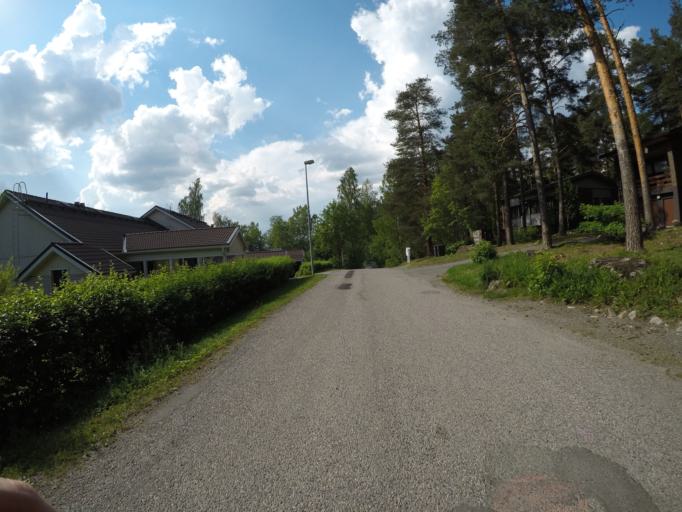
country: FI
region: Haeme
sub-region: Haemeenlinna
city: Haemeenlinna
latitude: 61.0089
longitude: 24.4675
